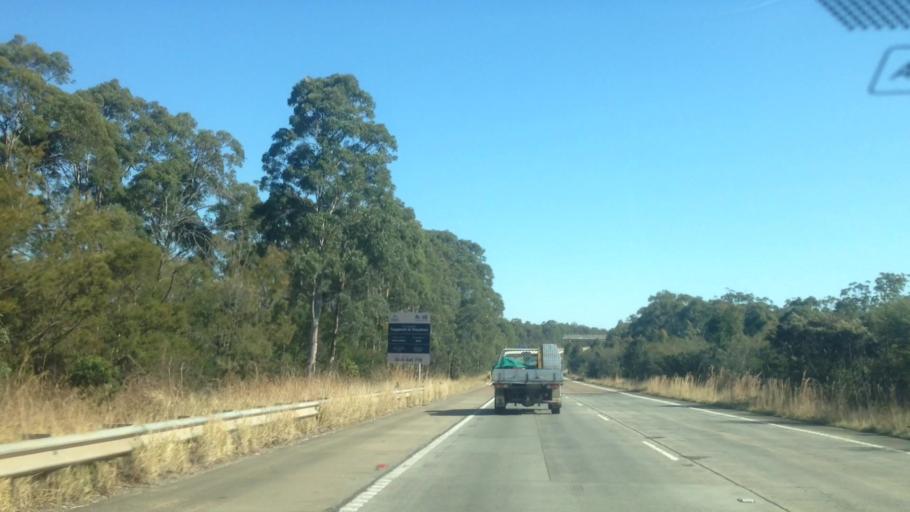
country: AU
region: New South Wales
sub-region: Wyong Shire
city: Jilliby
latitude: -33.2099
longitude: 151.4536
